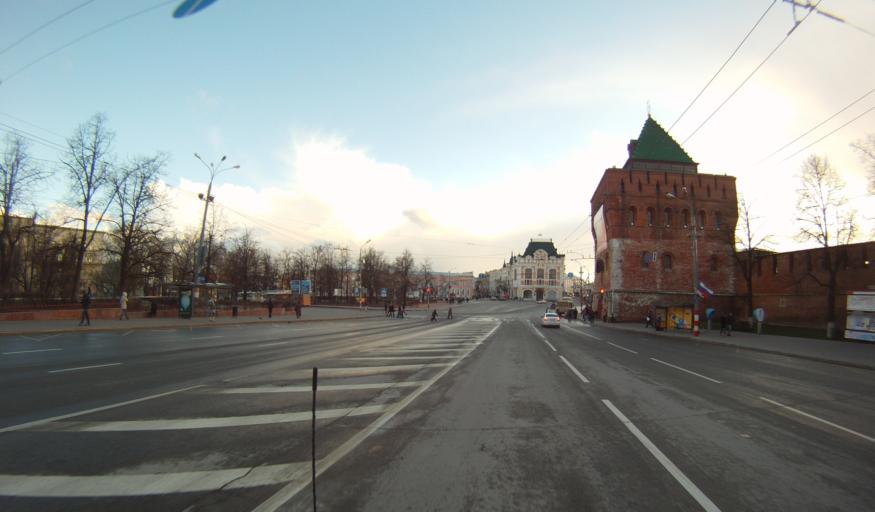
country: RU
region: Nizjnij Novgorod
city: Nizhniy Novgorod
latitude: 56.3274
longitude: 44.0065
